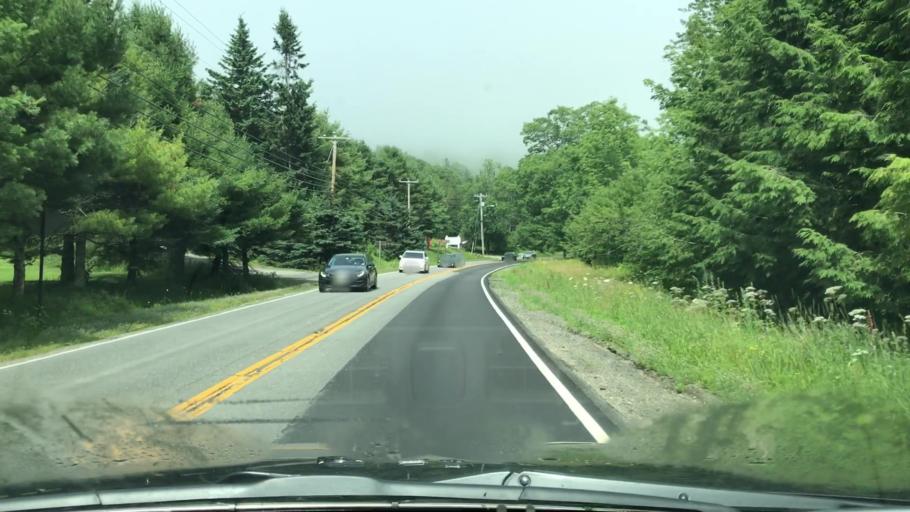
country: US
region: Maine
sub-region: Waldo County
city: Lincolnville
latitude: 44.2956
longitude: -69.0073
